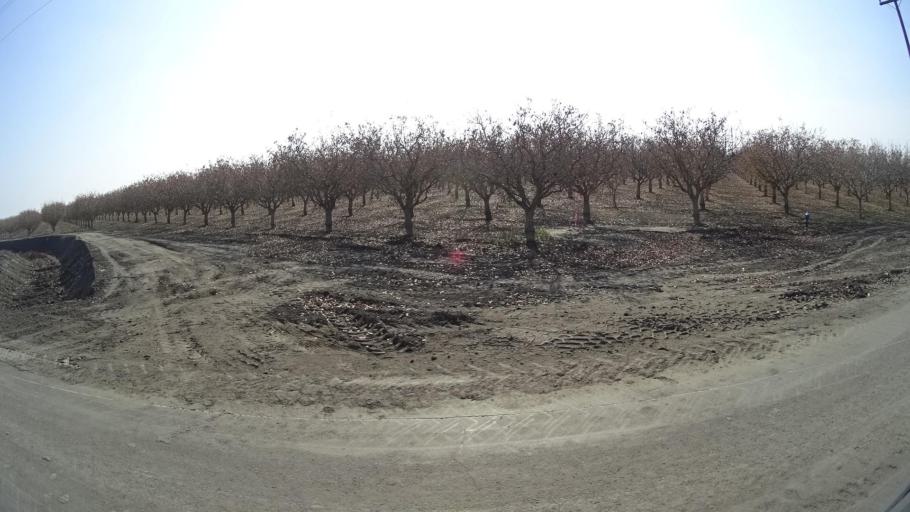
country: US
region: California
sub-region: Kern County
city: Buttonwillow
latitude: 35.3693
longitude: -119.4377
